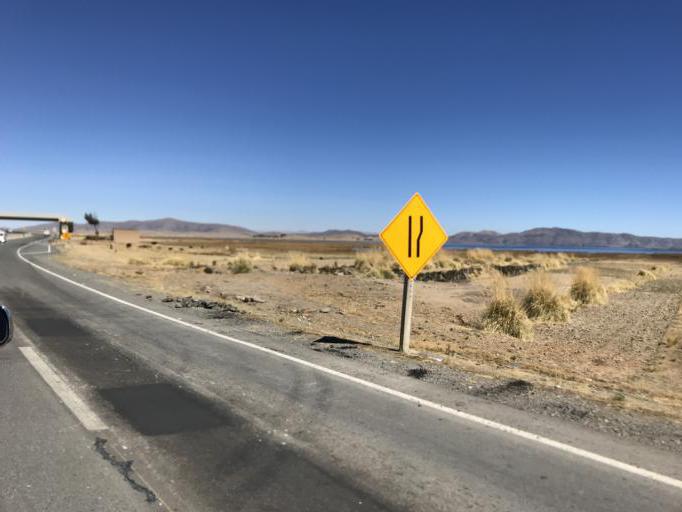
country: BO
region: La Paz
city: Huarina
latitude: -16.2360
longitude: -68.5772
